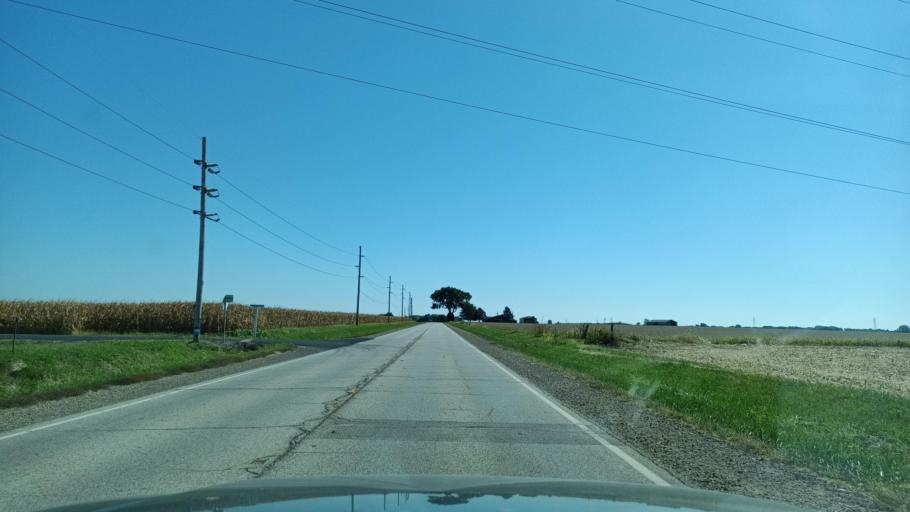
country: US
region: Illinois
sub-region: Peoria County
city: Dunlap
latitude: 40.7878
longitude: -89.7378
